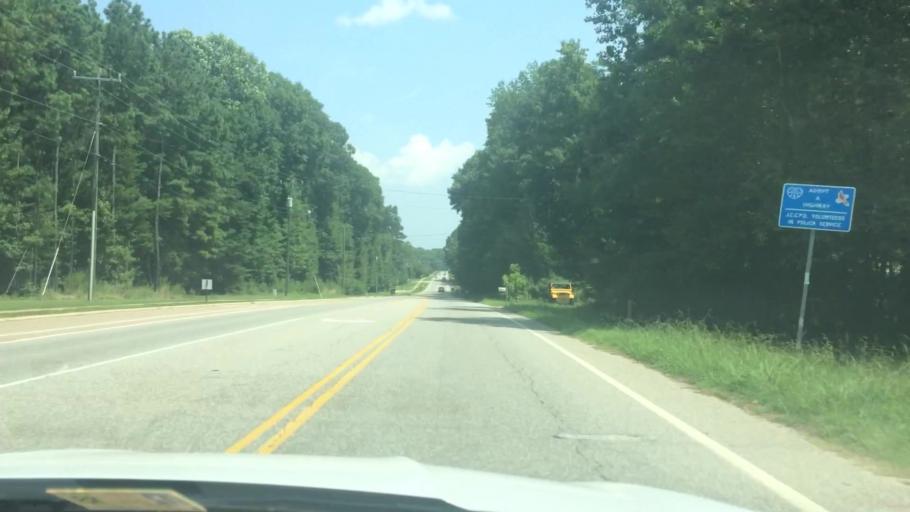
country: US
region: Virginia
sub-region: James City County
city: Williamsburg
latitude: 37.3351
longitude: -76.7750
